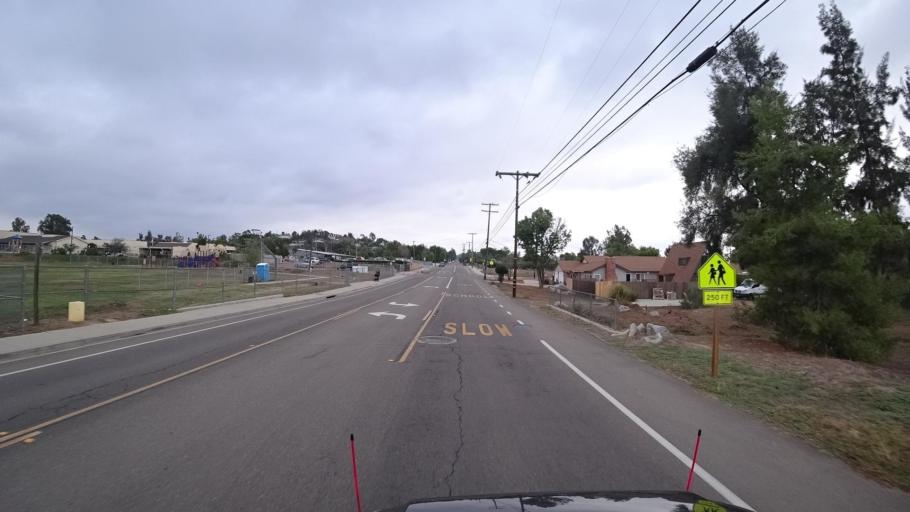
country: US
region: California
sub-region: San Diego County
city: Ramona
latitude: 33.0275
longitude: -116.8795
